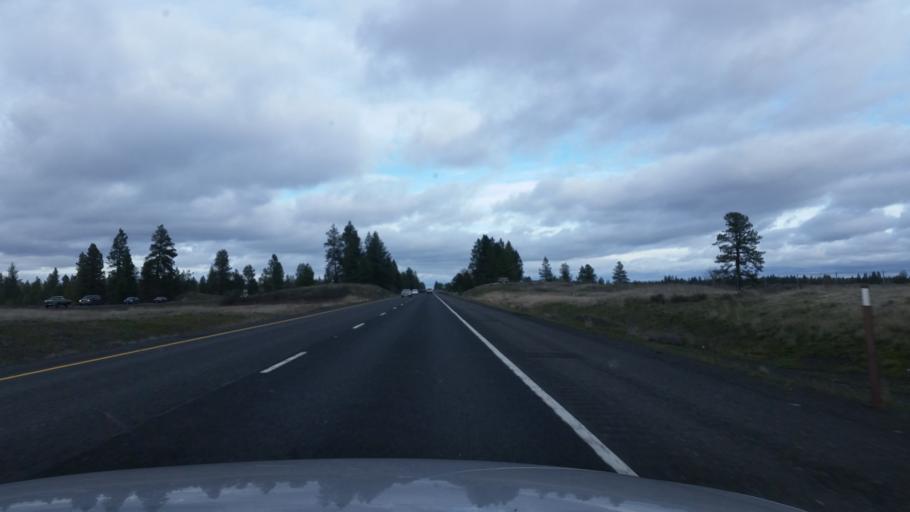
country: US
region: Washington
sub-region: Spokane County
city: Medical Lake
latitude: 47.4077
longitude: -117.8253
